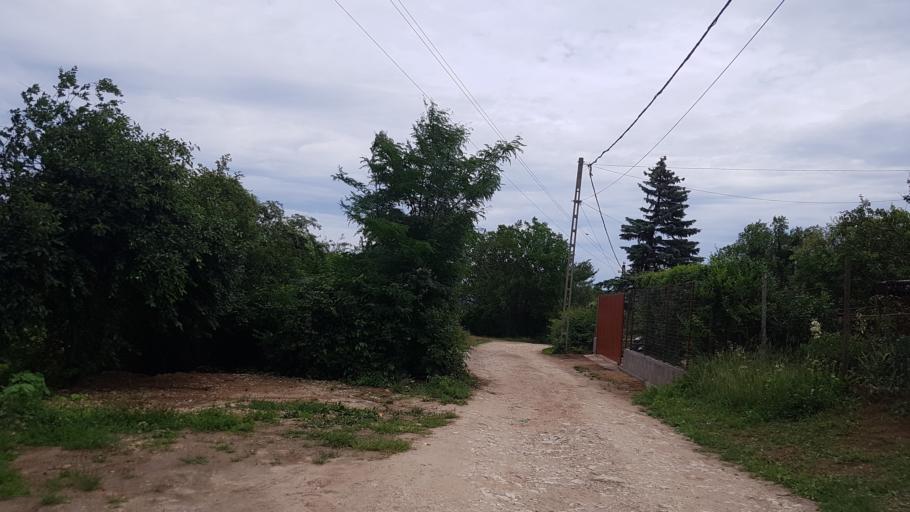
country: HU
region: Pest
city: Urom
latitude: 47.6086
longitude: 19.0290
